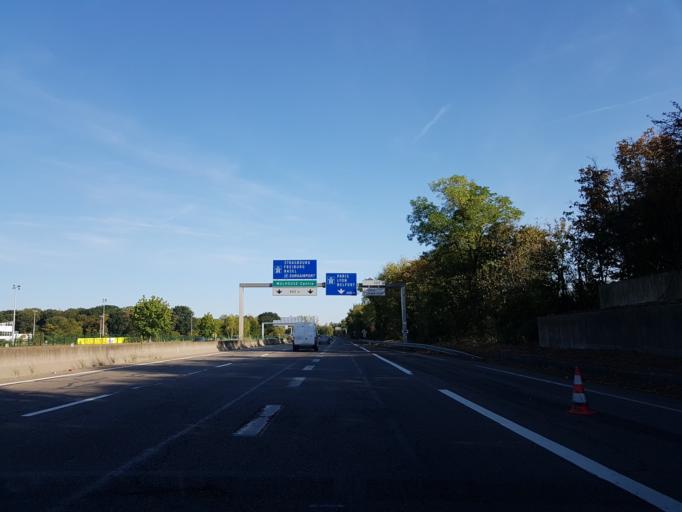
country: FR
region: Alsace
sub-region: Departement du Haut-Rhin
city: Illzach
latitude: 47.7756
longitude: 7.3349
